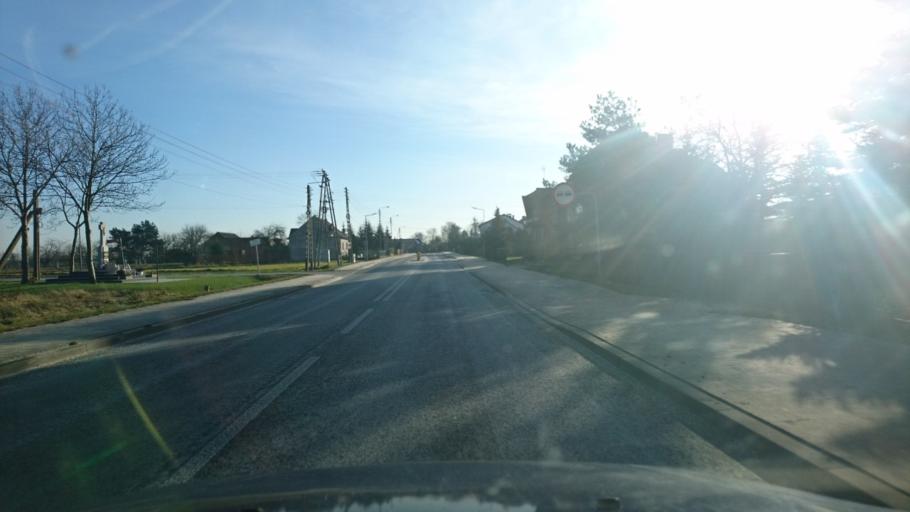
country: PL
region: Silesian Voivodeship
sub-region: Powiat klobucki
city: Starokrzepice
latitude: 51.0074
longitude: 18.6583
